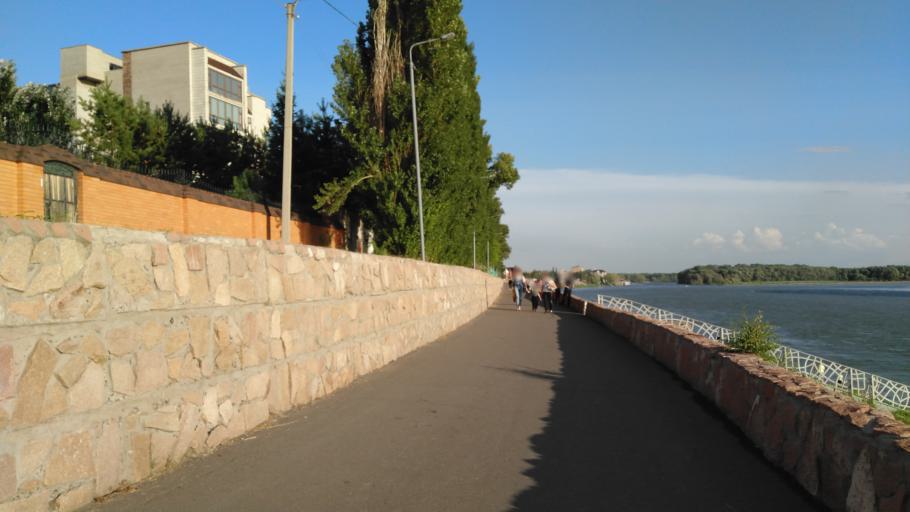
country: KZ
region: Pavlodar
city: Pavlodar
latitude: 52.2773
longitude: 76.9332
